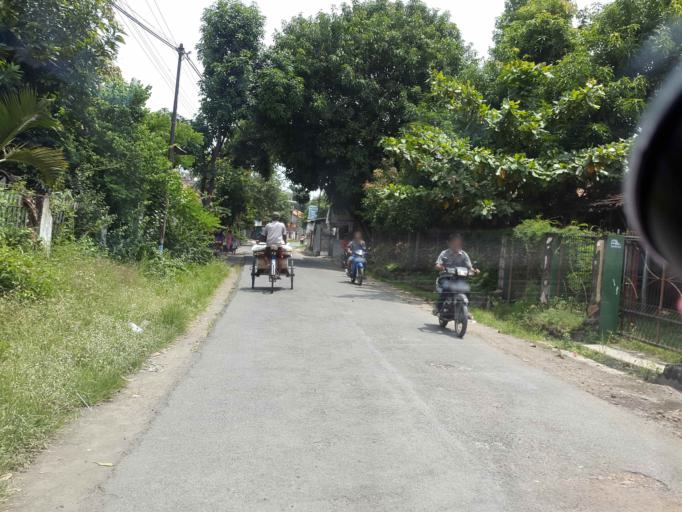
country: ID
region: Central Java
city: Petarukan
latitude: -6.8938
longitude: 109.4149
